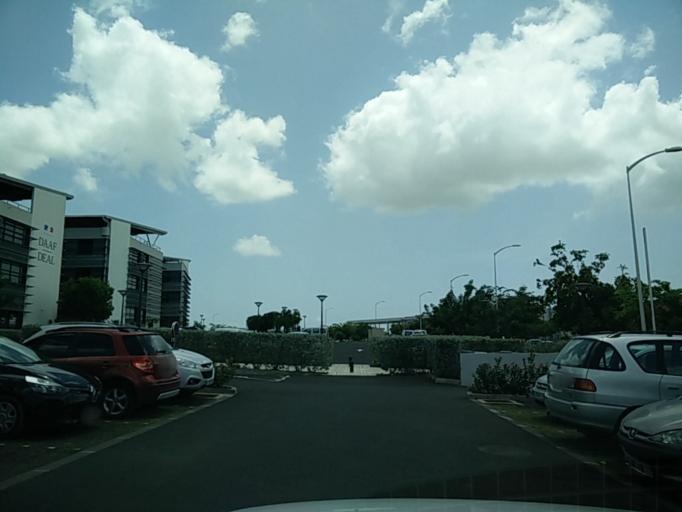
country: GP
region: Guadeloupe
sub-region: Guadeloupe
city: Les Abymes
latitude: 16.2758
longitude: -61.5103
